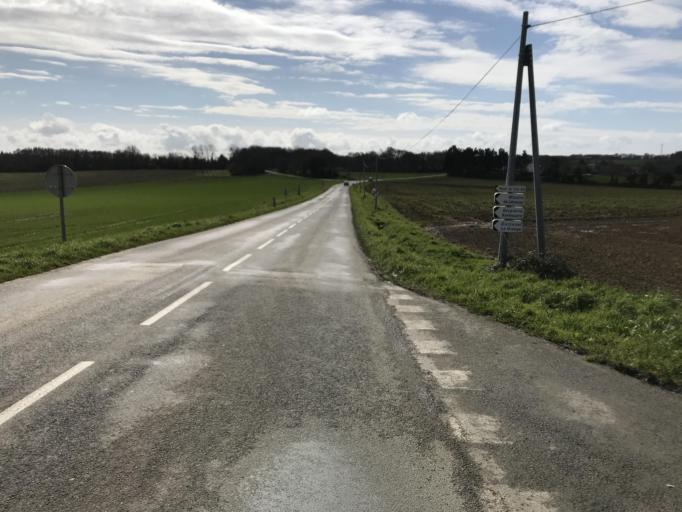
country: FR
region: Brittany
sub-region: Departement du Finistere
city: Dirinon
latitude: 48.3876
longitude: -4.2666
